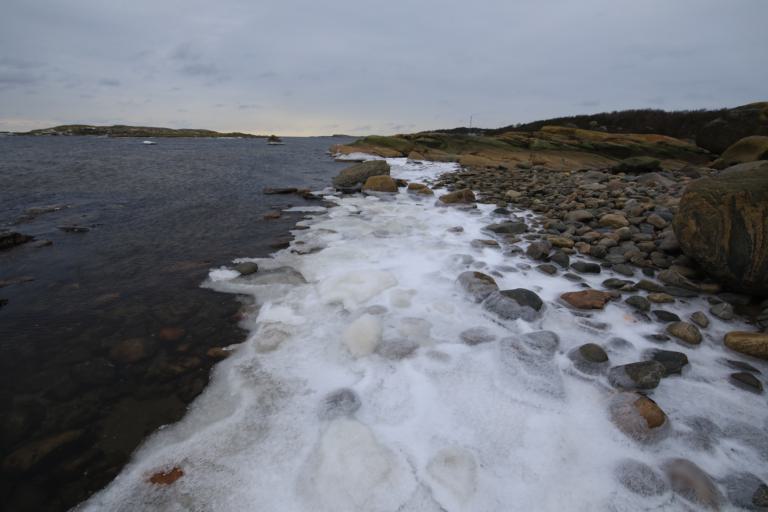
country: SE
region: Halland
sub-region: Kungsbacka Kommun
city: Frillesas
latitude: 57.2137
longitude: 12.1702
